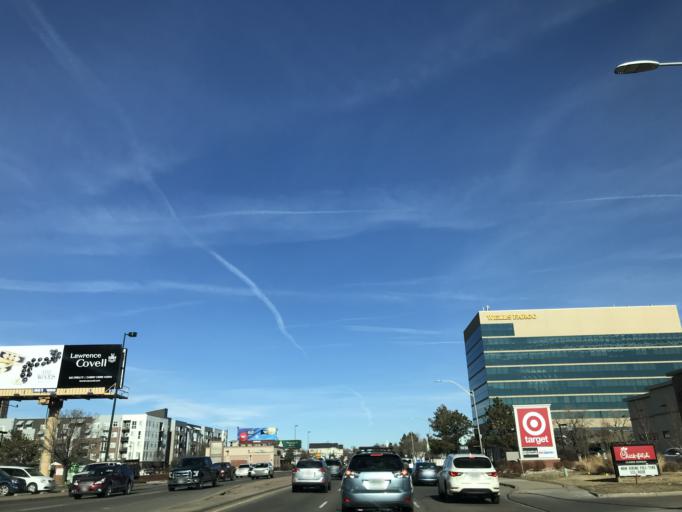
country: US
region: Colorado
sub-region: Arapahoe County
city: Glendale
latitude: 39.7079
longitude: -104.9407
